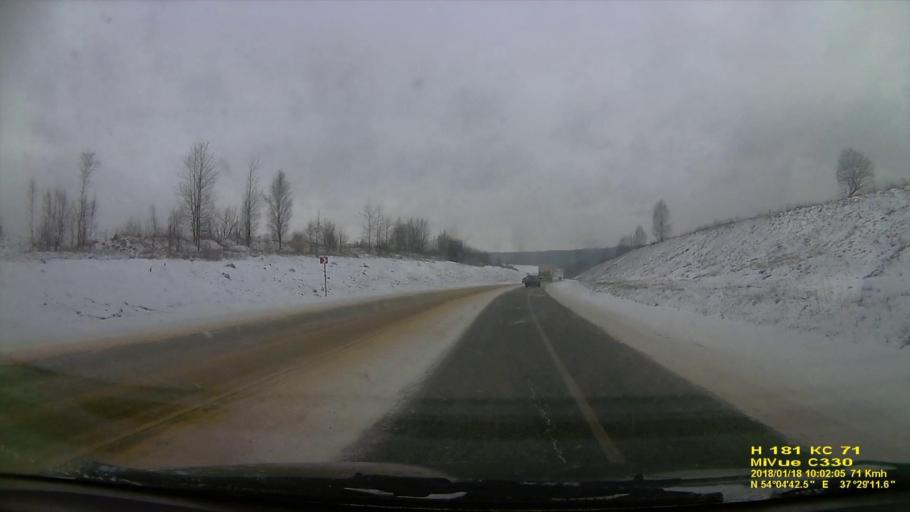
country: RU
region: Tula
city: Pervomayskiy
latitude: 54.0783
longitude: 37.4863
